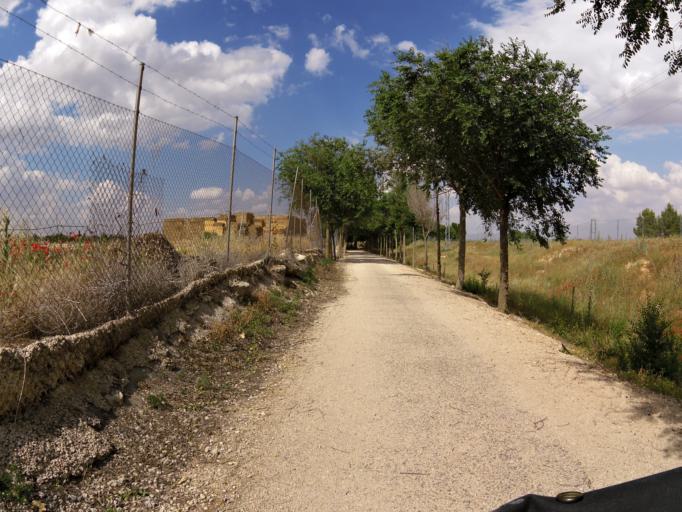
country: ES
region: Castille-La Mancha
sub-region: Provincia de Albacete
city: Albacete
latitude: 38.9631
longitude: -1.9585
